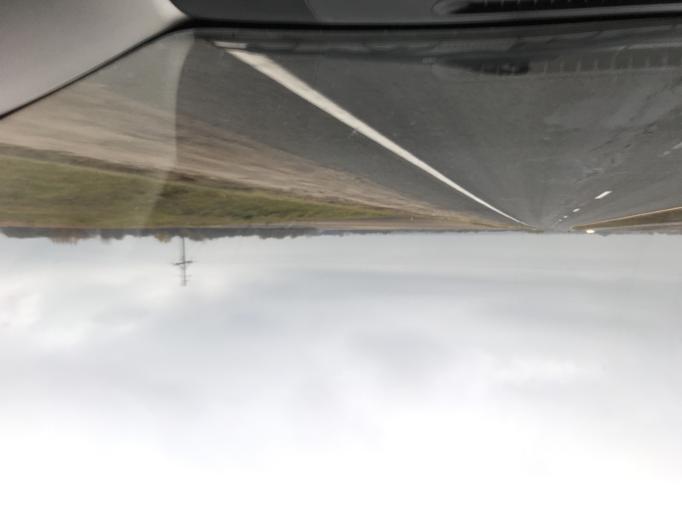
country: BY
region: Vitebsk
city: Vitebsk
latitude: 55.1551
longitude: 30.0914
